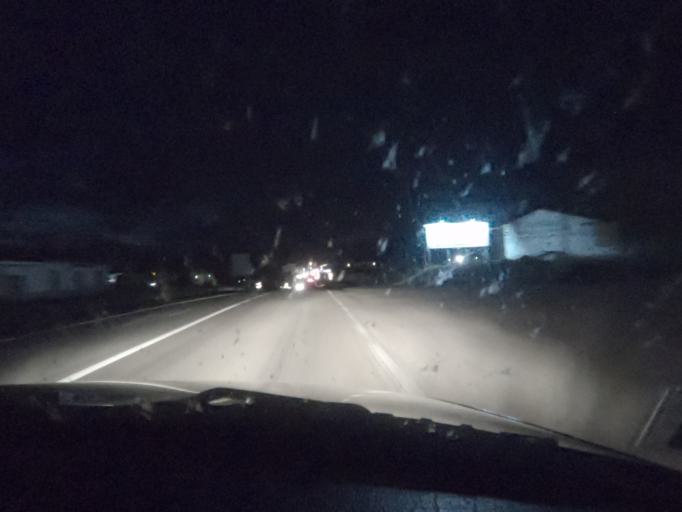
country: ES
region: Extremadura
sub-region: Provincia de Caceres
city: Moraleja
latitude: 40.0605
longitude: -6.6486
